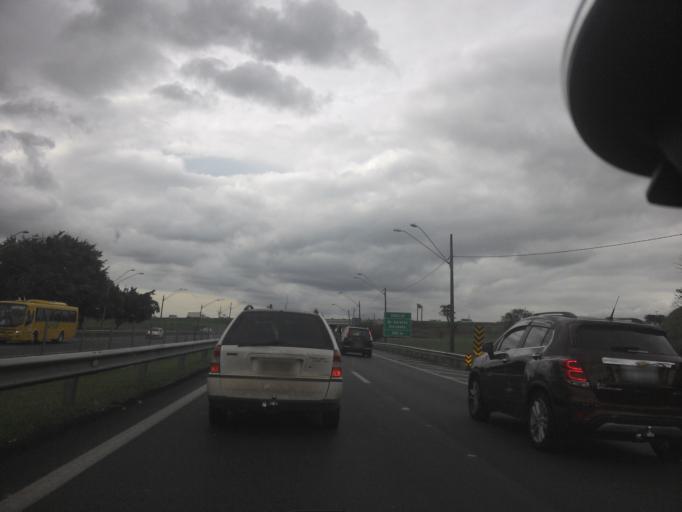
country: BR
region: Sao Paulo
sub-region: Campinas
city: Campinas
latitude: -22.8480
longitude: -47.0779
